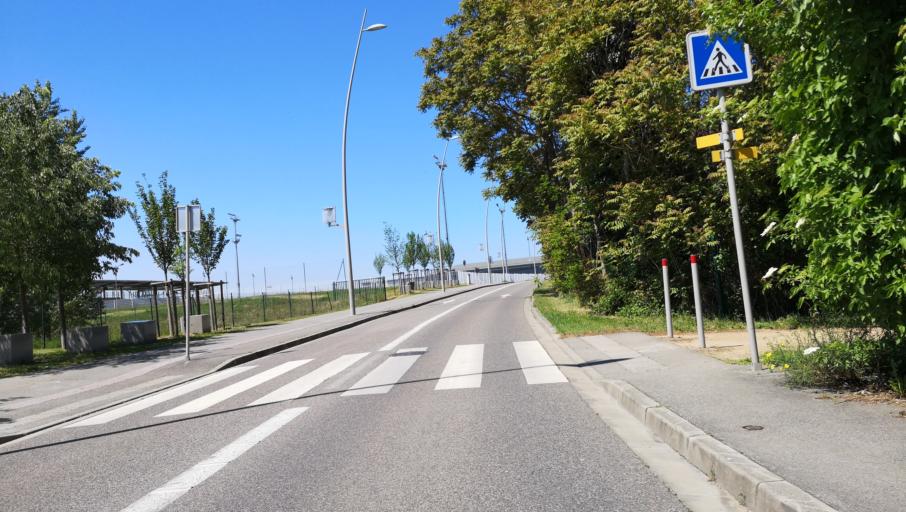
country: FR
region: Midi-Pyrenees
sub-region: Departement de la Haute-Garonne
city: Beauzelle
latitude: 43.6521
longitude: 1.3844
